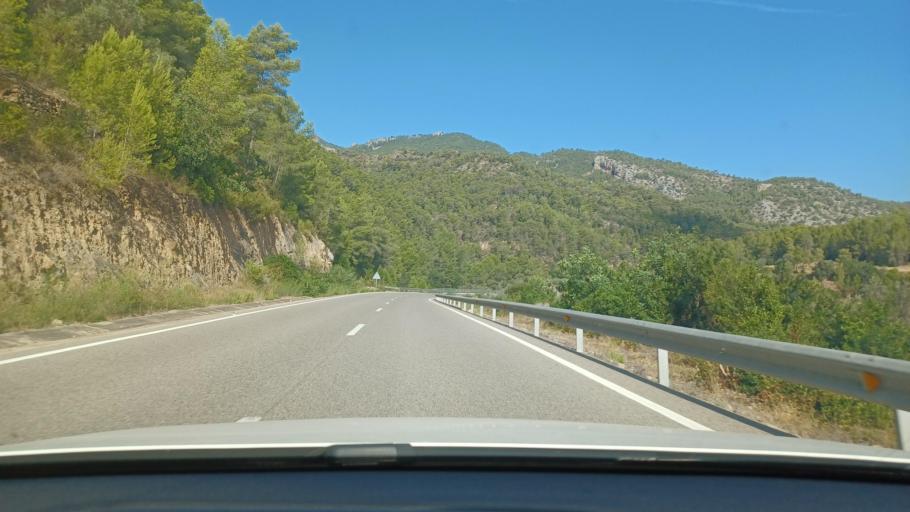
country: ES
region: Catalonia
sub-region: Provincia de Tarragona
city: Benifallet
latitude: 40.9518
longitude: 0.4497
